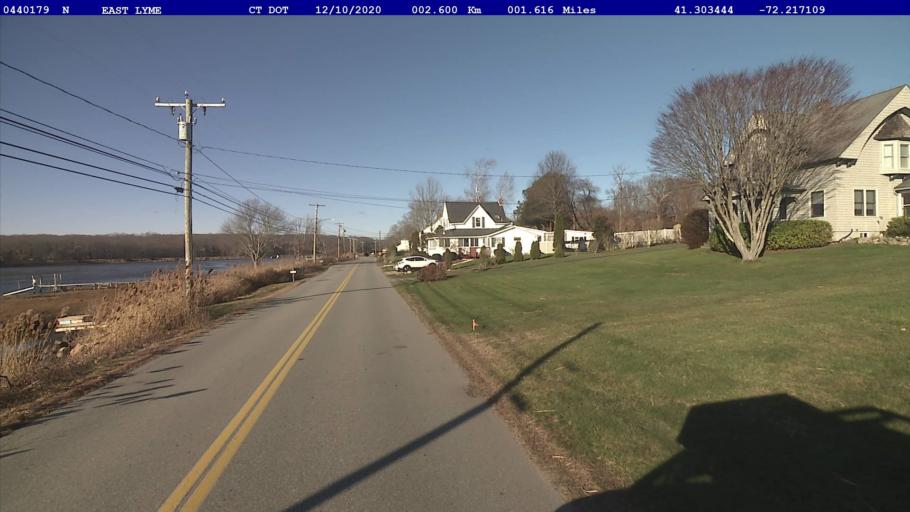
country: US
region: Connecticut
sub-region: New London County
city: Niantic
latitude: 41.3035
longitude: -72.2171
